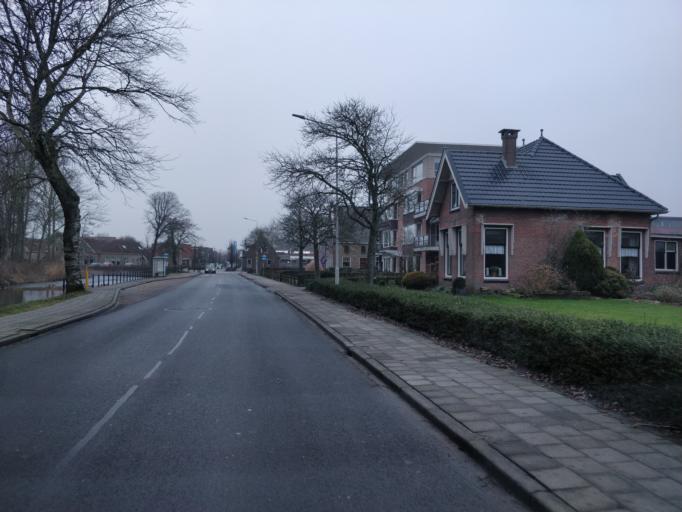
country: NL
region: Friesland
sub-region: Gemeente Het Bildt
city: Sint Annaparochie
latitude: 53.2736
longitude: 5.6578
